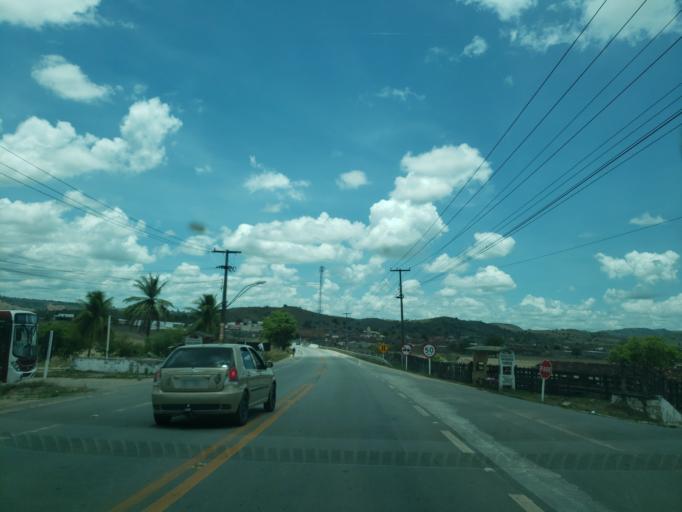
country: BR
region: Alagoas
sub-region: Uniao Dos Palmares
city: Uniao dos Palmares
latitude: -9.1563
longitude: -36.0133
